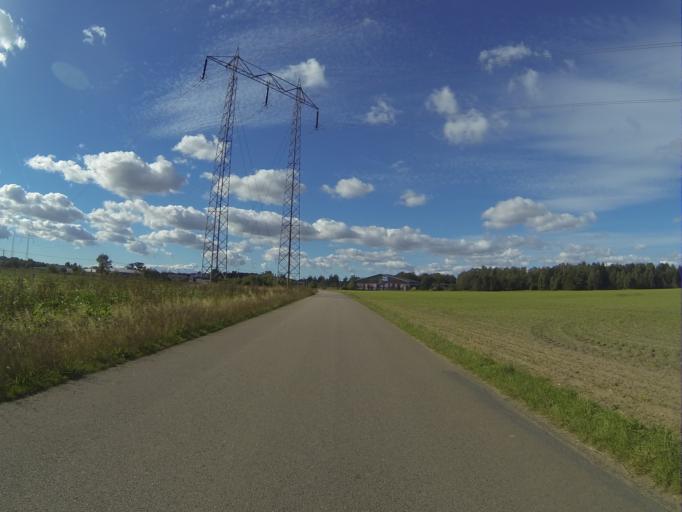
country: SE
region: Skane
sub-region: Lunds Kommun
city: Genarp
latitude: 55.7203
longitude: 13.3741
